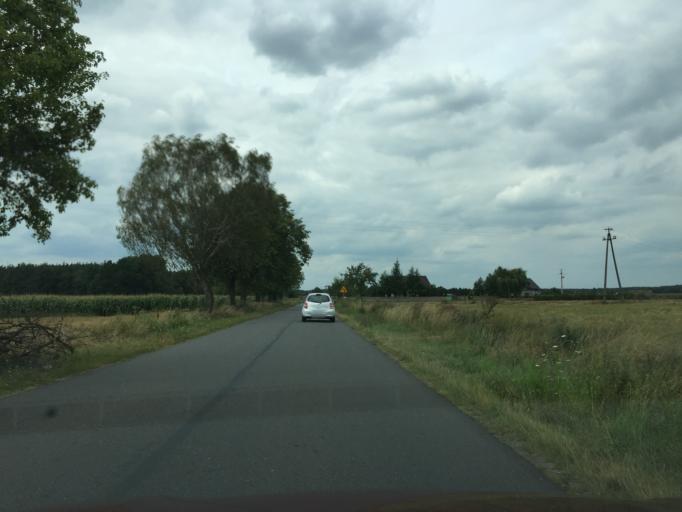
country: PL
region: Greater Poland Voivodeship
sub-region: Powiat kaliski
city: Stawiszyn
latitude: 51.9463
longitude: 18.1832
